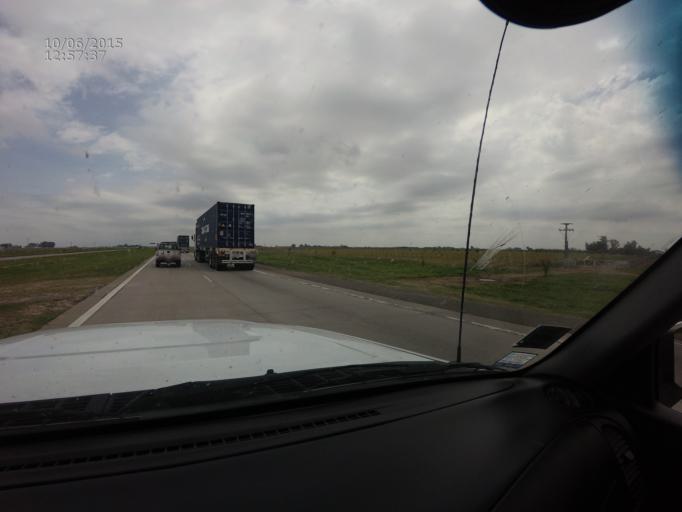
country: AR
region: Santa Fe
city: Armstrong
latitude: -32.8037
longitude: -61.6398
